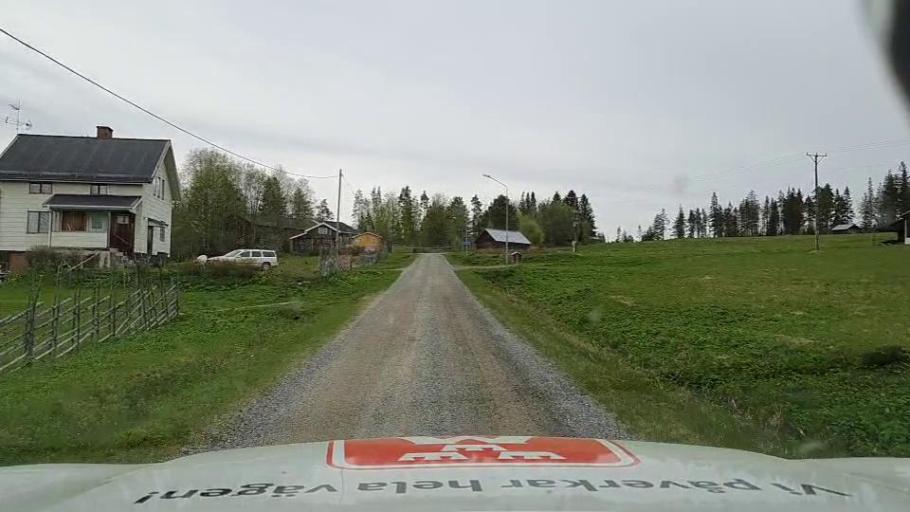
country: SE
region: Jaemtland
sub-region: Bergs Kommun
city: Hoverberg
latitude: 62.5717
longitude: 14.6662
